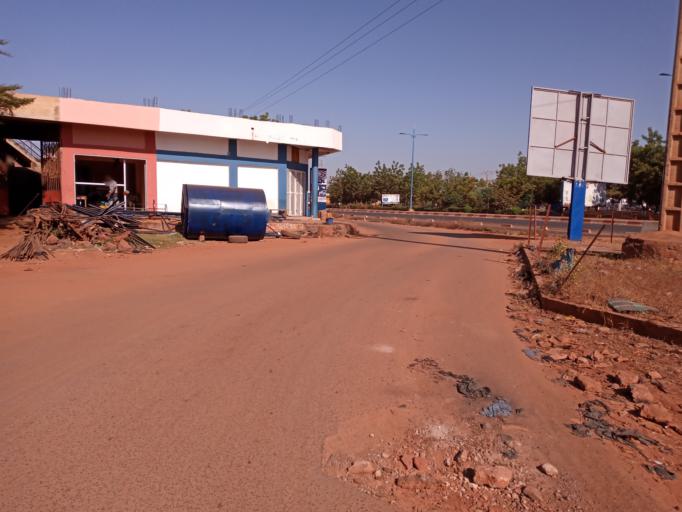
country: ML
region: Bamako
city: Bamako
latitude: 12.5989
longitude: -7.9626
